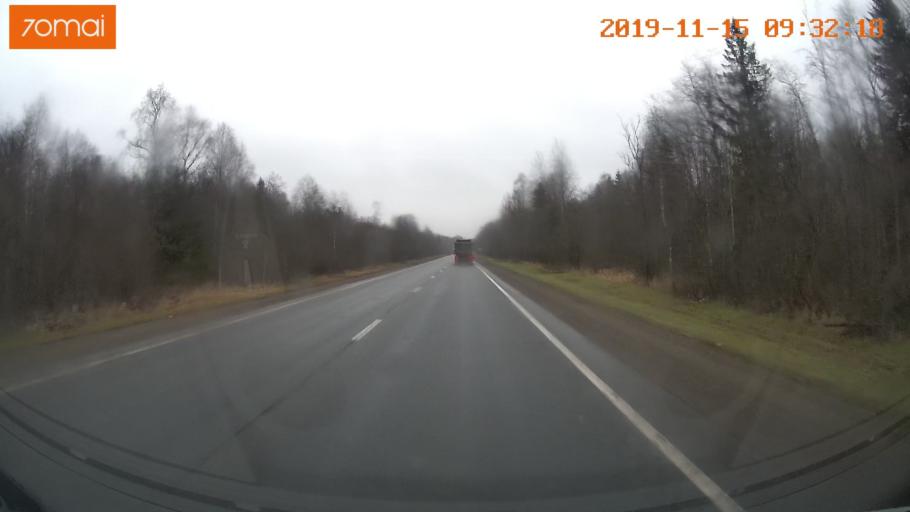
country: RU
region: Vologda
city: Sheksna
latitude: 59.2721
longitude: 38.3315
